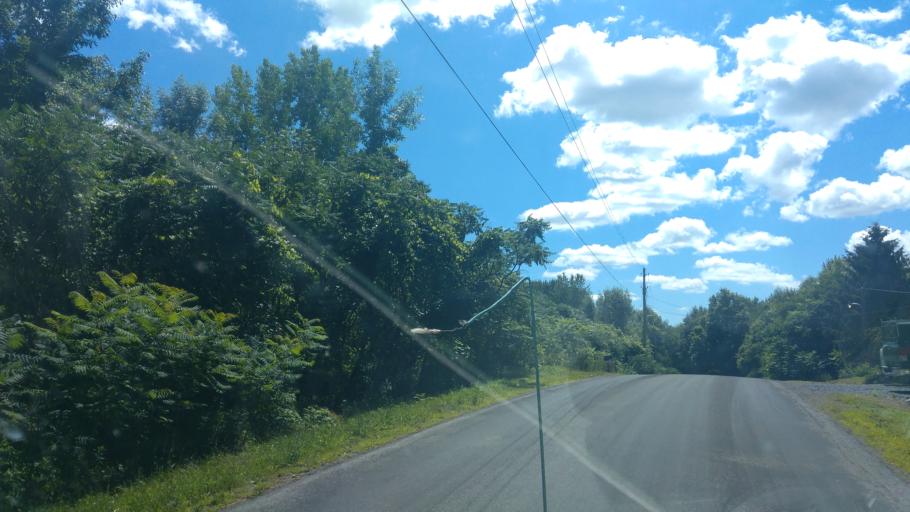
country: US
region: New York
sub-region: Wayne County
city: Lyons
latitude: 43.1492
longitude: -76.9652
